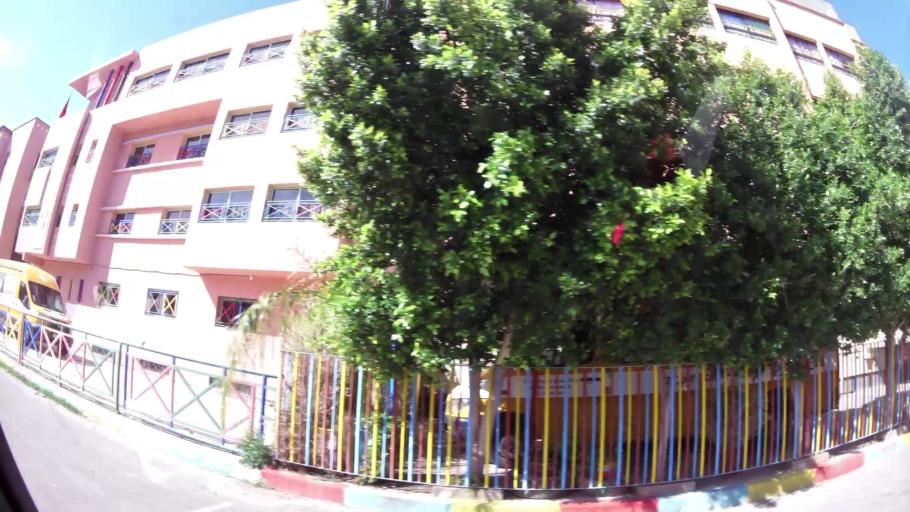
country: MA
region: Marrakech-Tensift-Al Haouz
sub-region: Marrakech
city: Marrakesh
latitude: 31.6682
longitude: -8.0226
